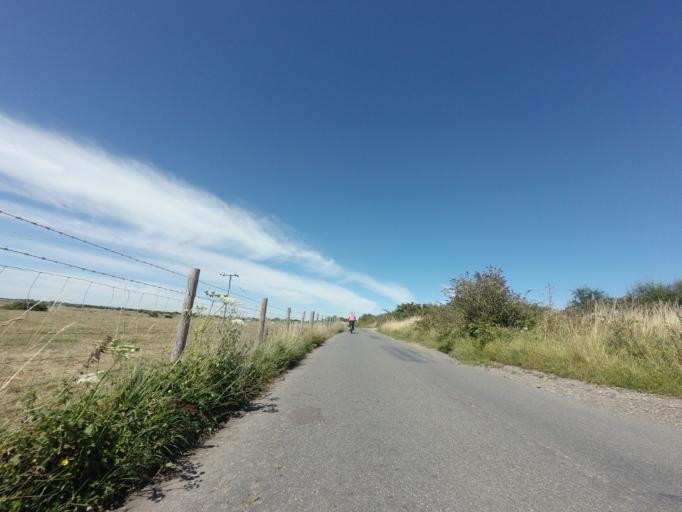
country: GB
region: England
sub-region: Kent
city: Deal
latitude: 51.2433
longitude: 1.3960
